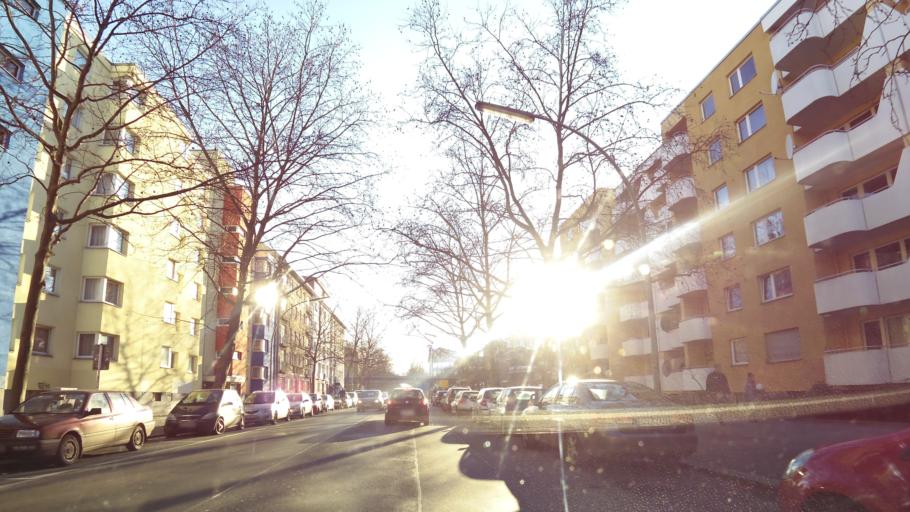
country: DE
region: Berlin
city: Bezirk Kreuzberg
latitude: 52.4995
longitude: 13.4074
